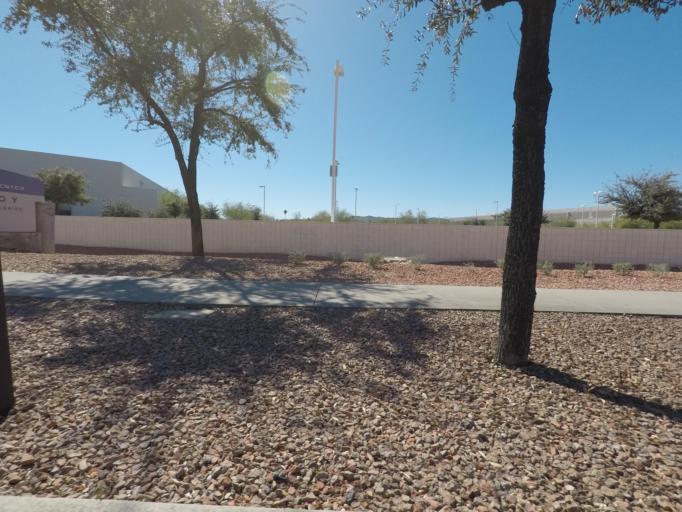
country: US
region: Arizona
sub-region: Maricopa County
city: Guadalupe
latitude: 33.4023
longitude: -111.9904
